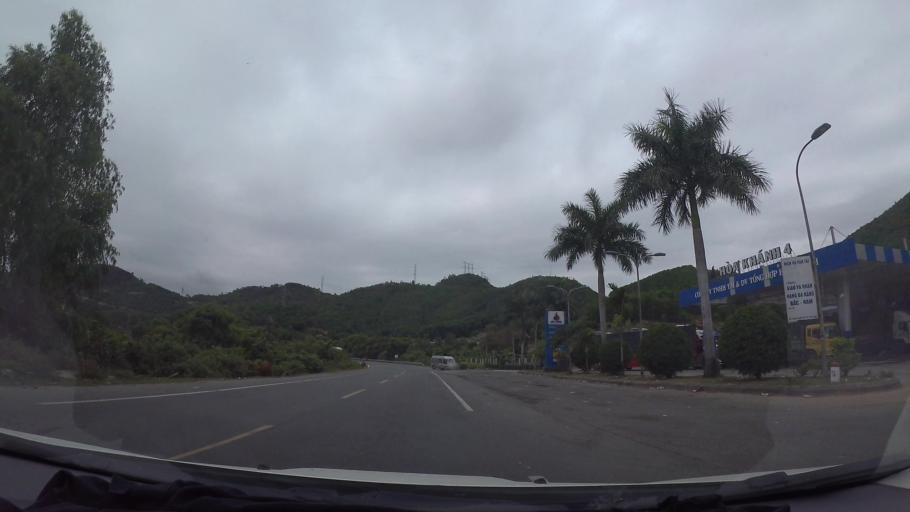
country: VN
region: Da Nang
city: Lien Chieu
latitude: 16.1293
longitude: 108.1012
